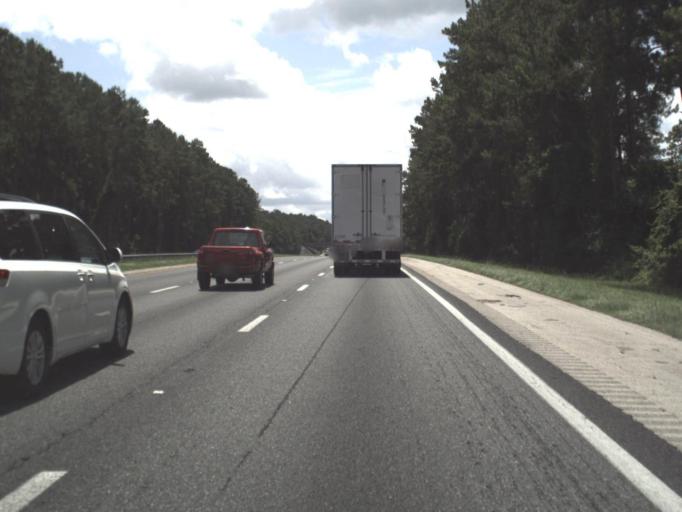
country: US
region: Florida
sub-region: Alachua County
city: Alachua
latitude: 29.7221
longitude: -82.4692
